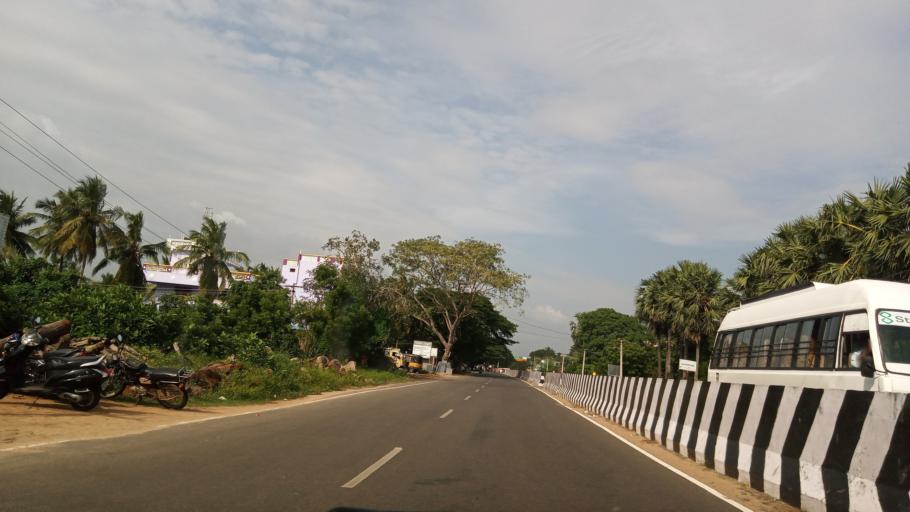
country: IN
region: Tamil Nadu
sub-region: Villupuram
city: Auroville
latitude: 12.0536
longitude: 79.8732
